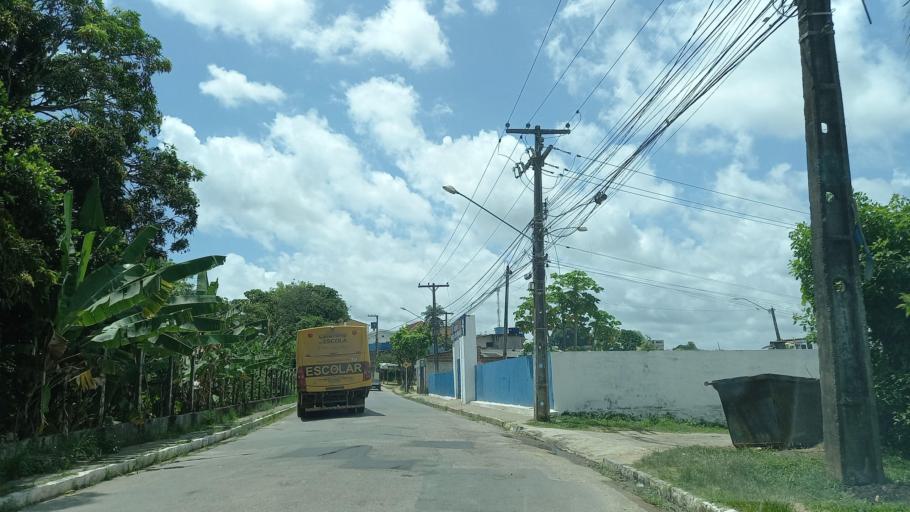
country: BR
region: Pernambuco
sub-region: Jaboatao Dos Guararapes
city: Jaboatao
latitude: -8.1693
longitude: -34.9979
